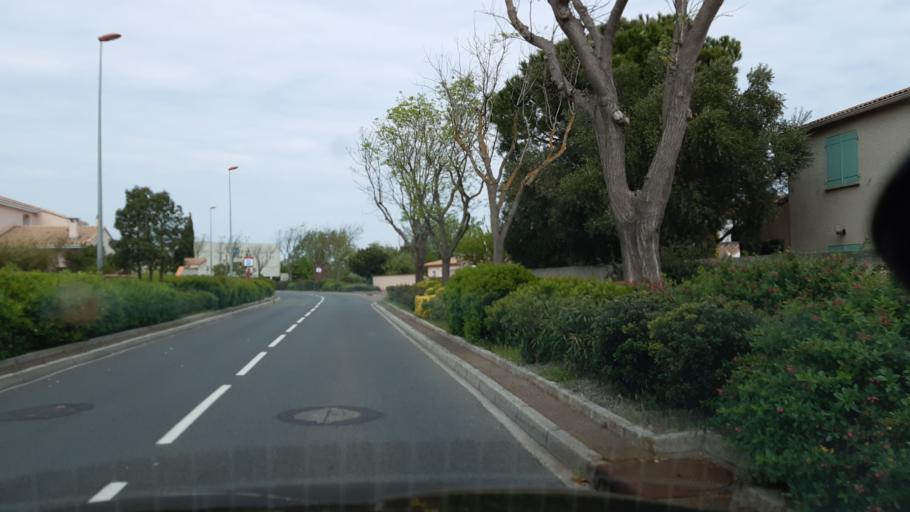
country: FR
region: Languedoc-Roussillon
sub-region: Departement de l'Aude
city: Narbonne
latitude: 43.1851
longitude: 3.0318
